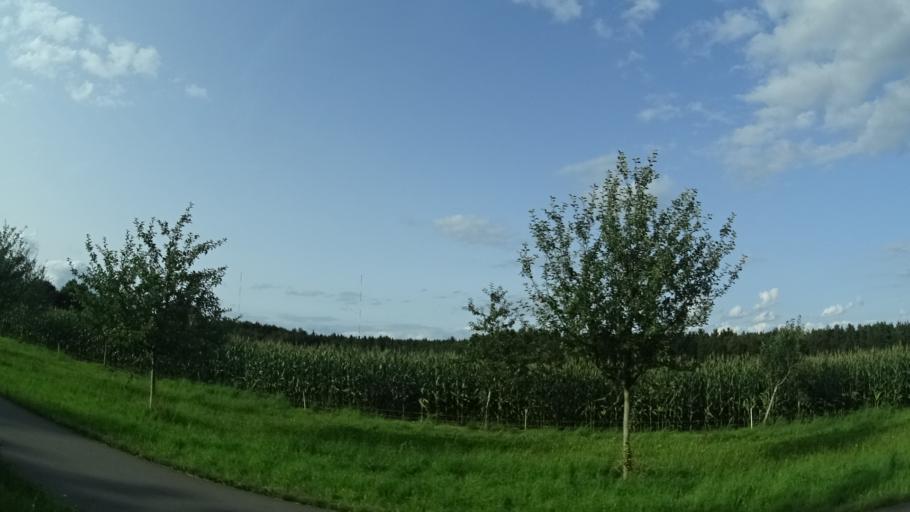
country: DE
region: Baden-Wuerttemberg
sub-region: Karlsruhe Region
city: Mudau
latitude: 49.5385
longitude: 9.1802
